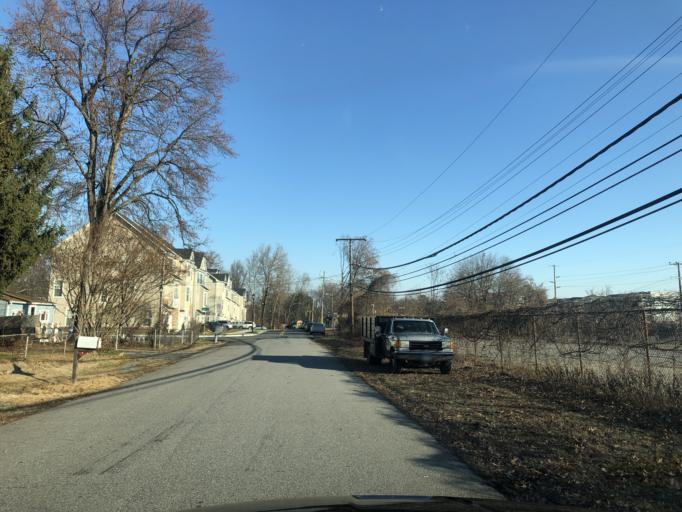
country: US
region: Maryland
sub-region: Anne Arundel County
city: Odenton
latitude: 39.0903
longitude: -76.6979
